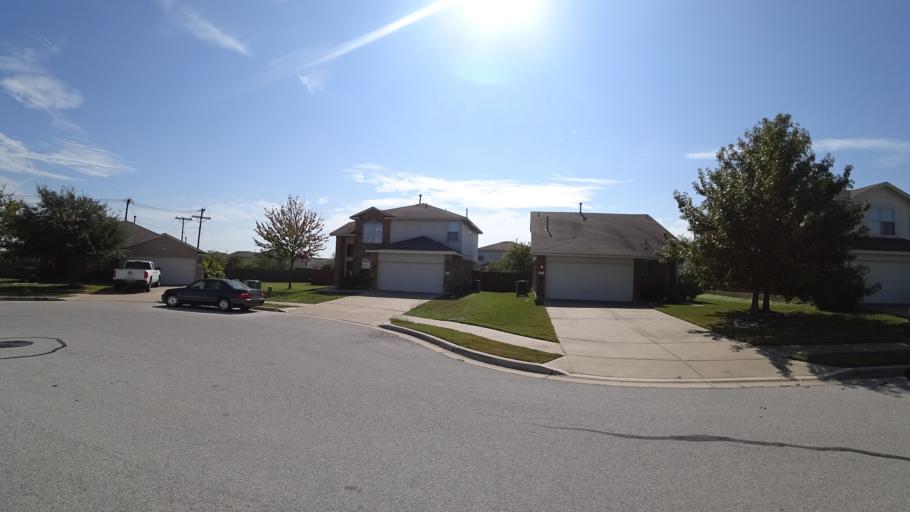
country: US
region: Texas
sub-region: Travis County
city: Pflugerville
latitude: 30.4289
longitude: -97.6380
